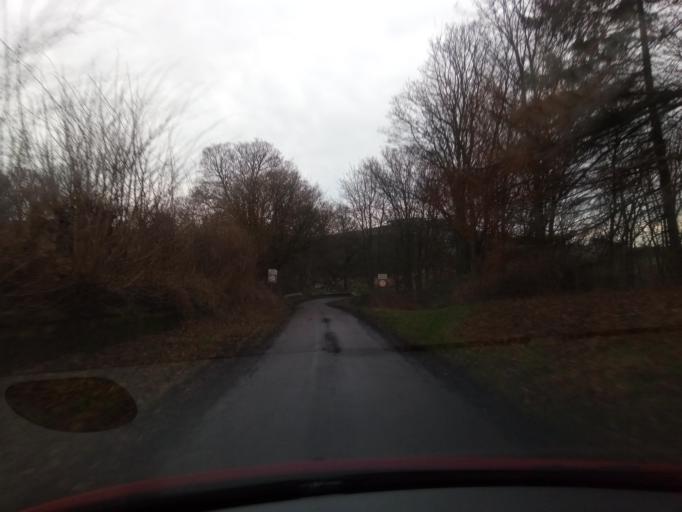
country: GB
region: England
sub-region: Northumberland
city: Wooler
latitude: 55.4958
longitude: -1.9125
